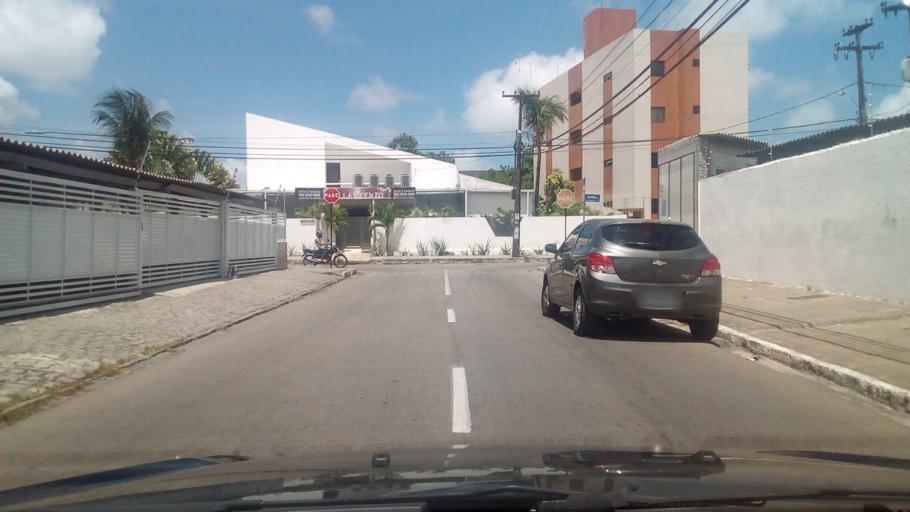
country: BR
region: Paraiba
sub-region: Joao Pessoa
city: Joao Pessoa
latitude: -7.1536
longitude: -34.8360
